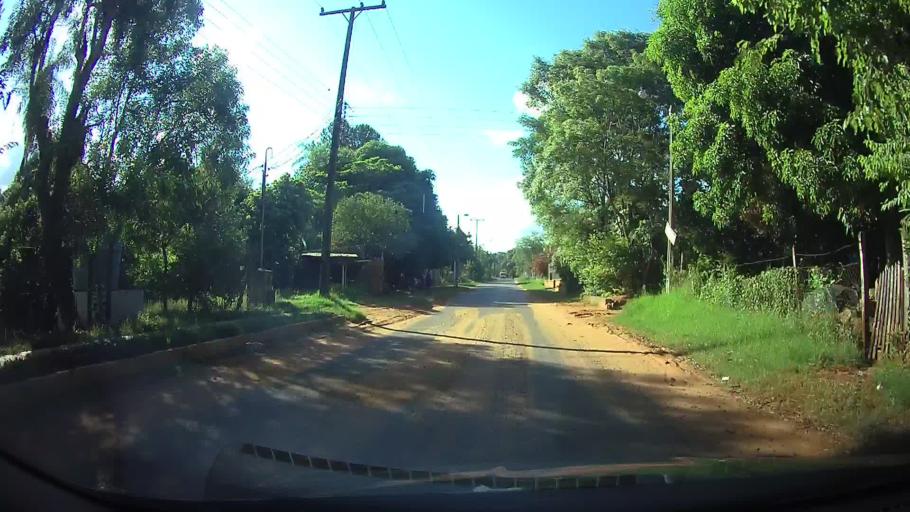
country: PY
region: Central
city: Aregua
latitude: -25.3570
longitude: -57.3897
